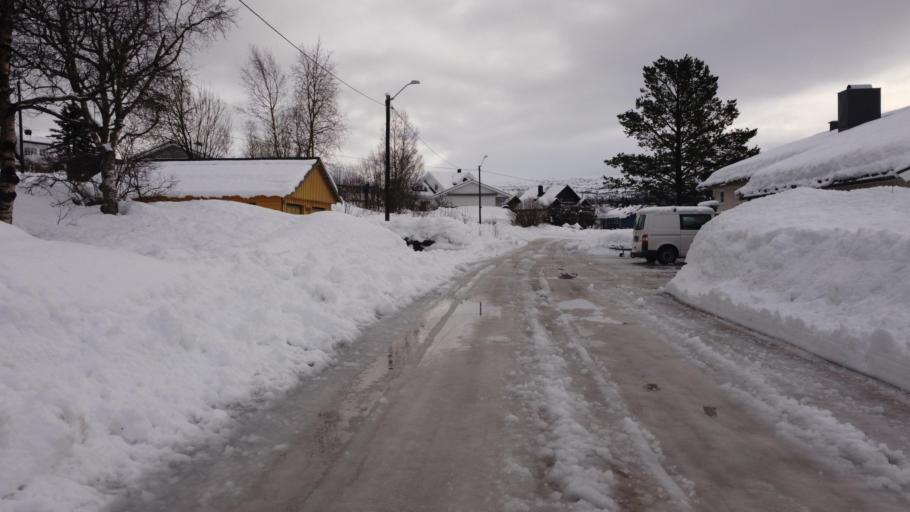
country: NO
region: Nordland
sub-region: Rana
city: Mo i Rana
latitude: 66.3336
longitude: 14.1495
